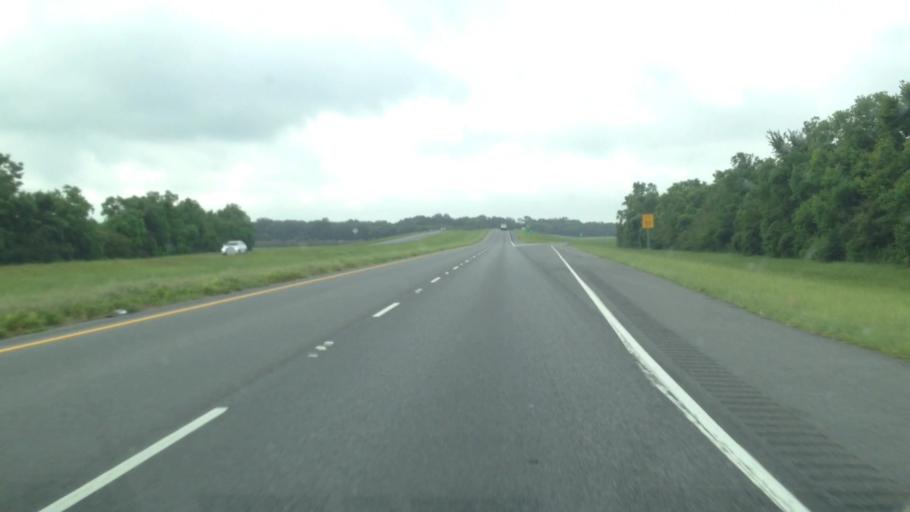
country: US
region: Louisiana
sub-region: Saint Landry Parish
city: Opelousas
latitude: 30.6467
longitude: -92.0540
